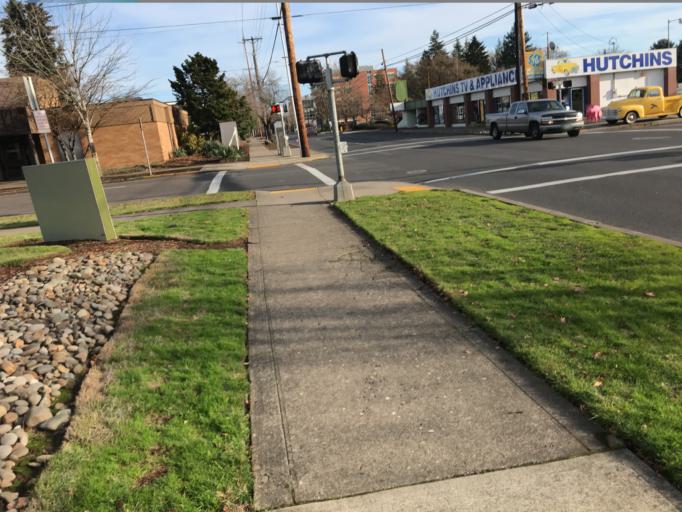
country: US
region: Oregon
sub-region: Washington County
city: Hillsboro
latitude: 45.5202
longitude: -122.9829
